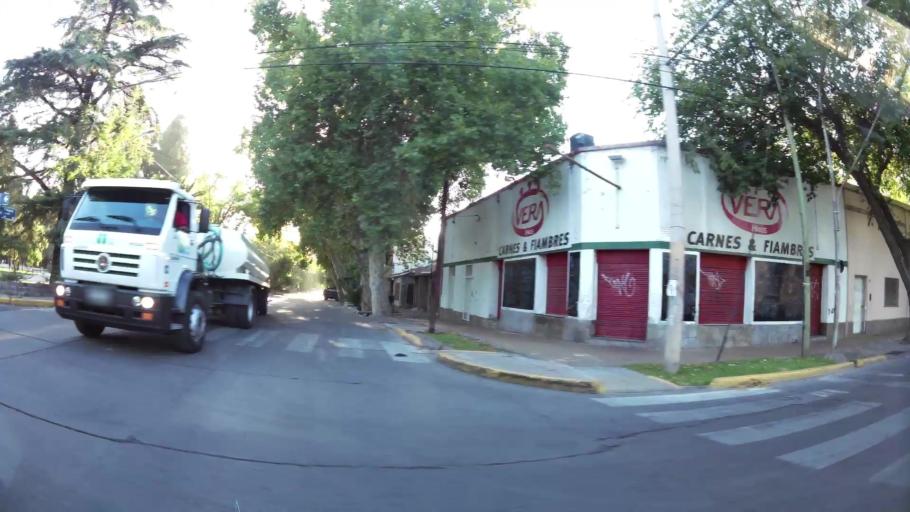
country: AR
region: Mendoza
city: Las Heras
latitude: -32.8700
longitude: -68.8392
